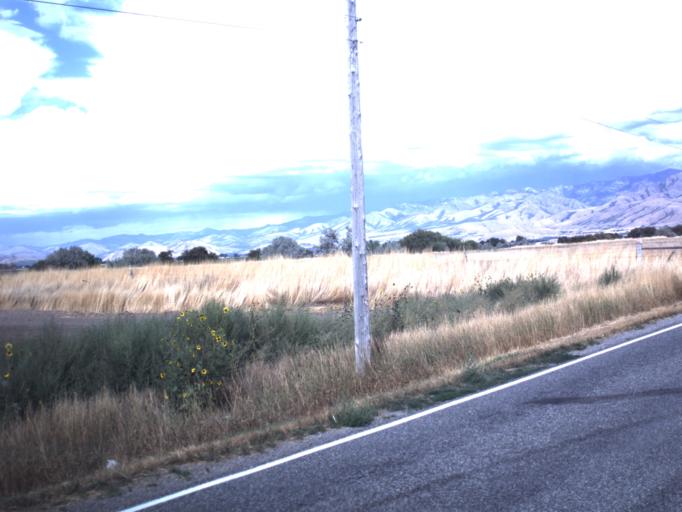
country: US
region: Utah
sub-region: Cache County
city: Lewiston
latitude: 41.9146
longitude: -111.9216
